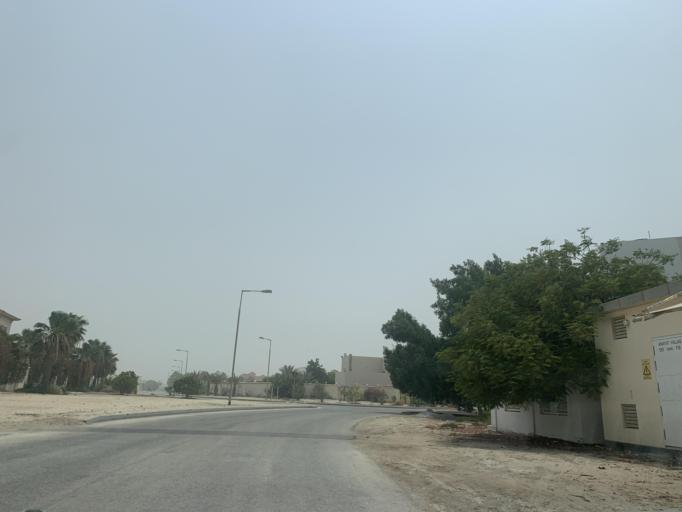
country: BH
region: Central Governorate
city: Madinat Hamad
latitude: 26.1644
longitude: 50.4767
